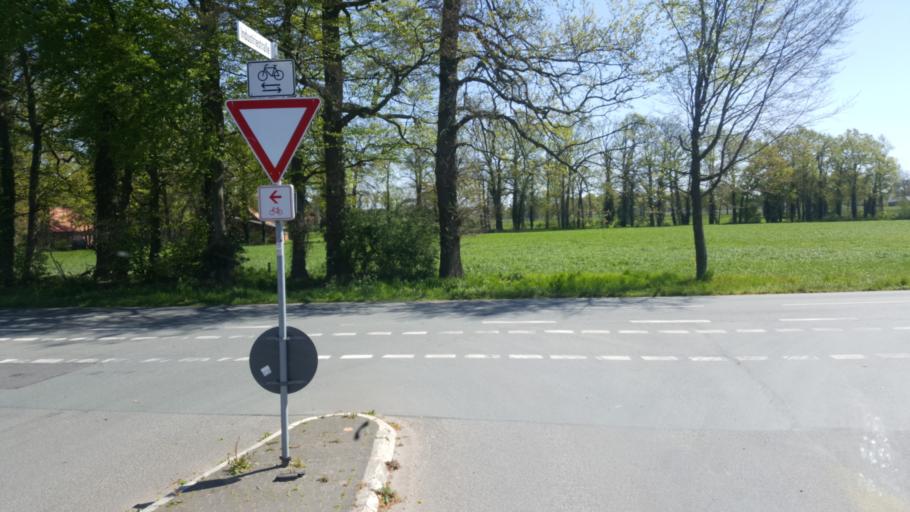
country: DE
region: North Rhine-Westphalia
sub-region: Regierungsbezirk Munster
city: Sudlohn
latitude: 51.9354
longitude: 6.8246
